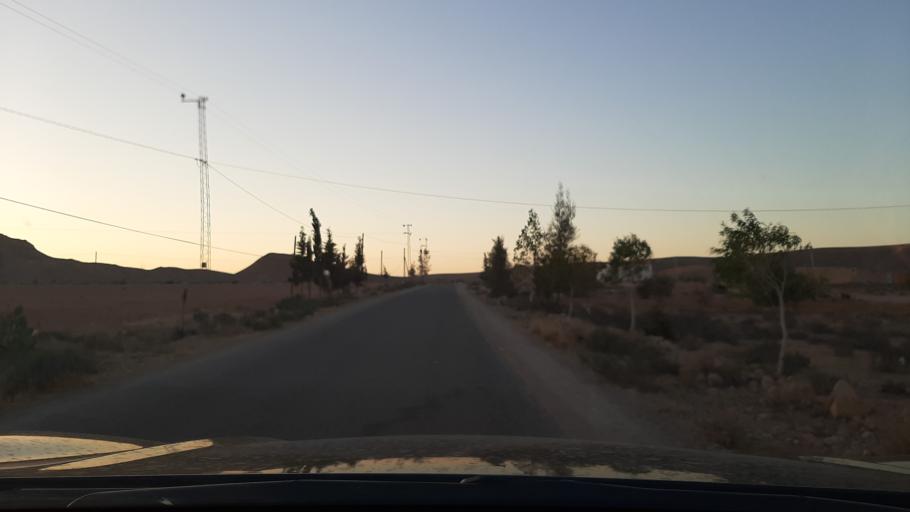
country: TN
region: Qabis
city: Matmata
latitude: 33.5679
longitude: 10.1775
